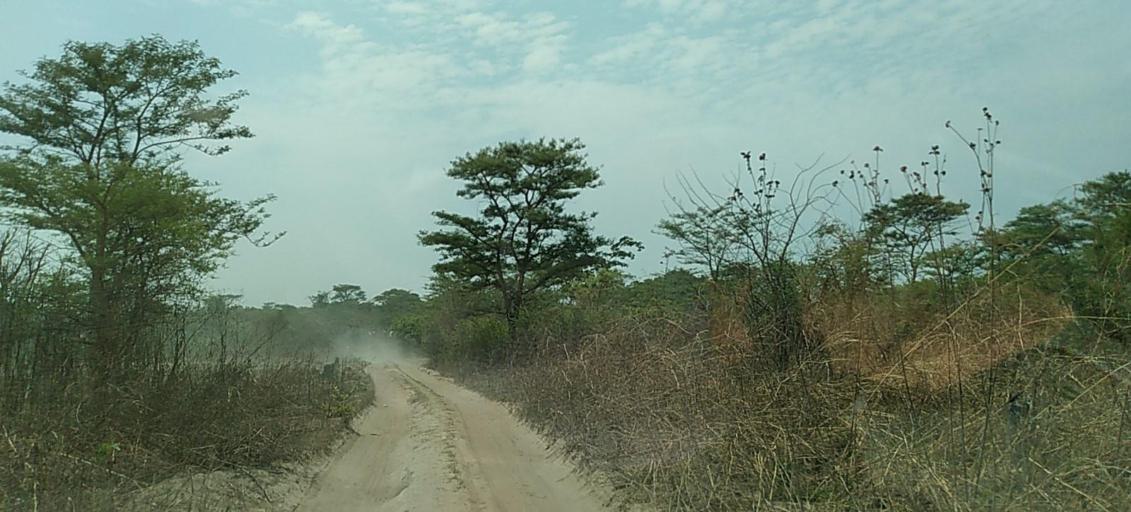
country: ZM
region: Copperbelt
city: Kalulushi
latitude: -12.9283
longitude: 28.1067
